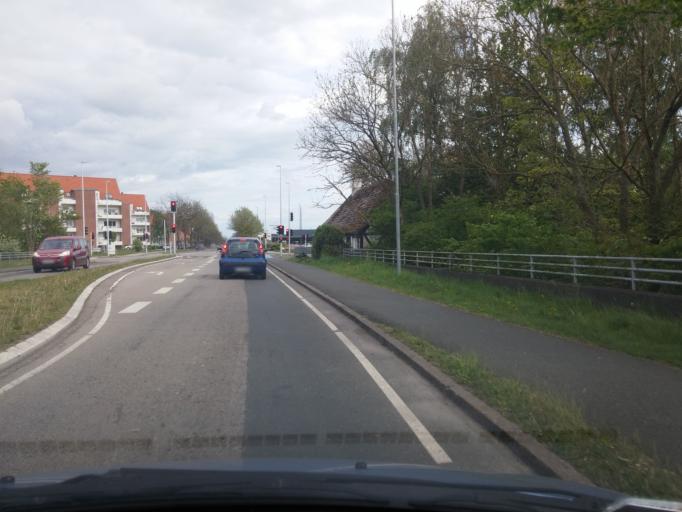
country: DK
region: South Denmark
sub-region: Nyborg Kommune
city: Nyborg
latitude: 55.3204
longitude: 10.7771
